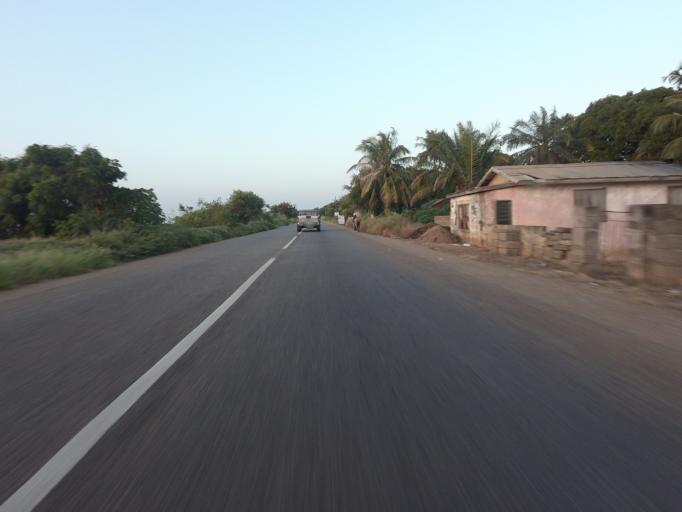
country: GH
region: Volta
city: Anloga
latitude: 5.8116
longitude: 0.9343
